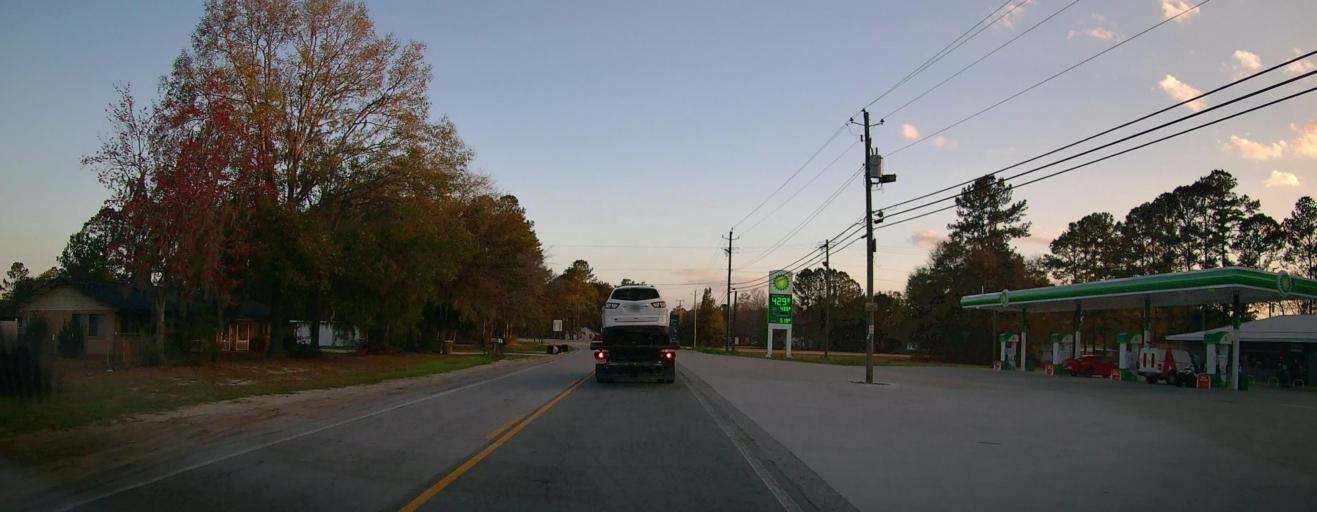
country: US
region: Georgia
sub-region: Chatham County
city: Bloomingdale
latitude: 32.1347
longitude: -81.3889
